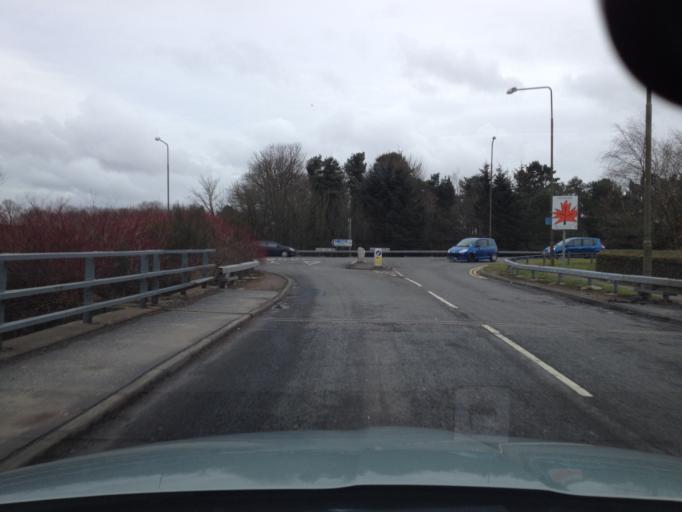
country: GB
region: Scotland
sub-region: West Lothian
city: Livingston
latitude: 55.8956
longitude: -3.5186
